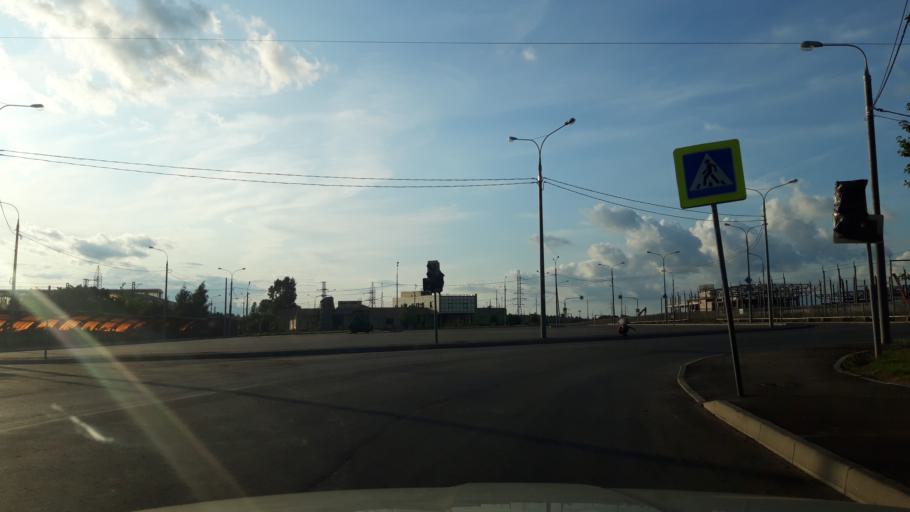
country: RU
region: Moskovskaya
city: Alabushevo
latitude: 56.0082
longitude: 37.1423
